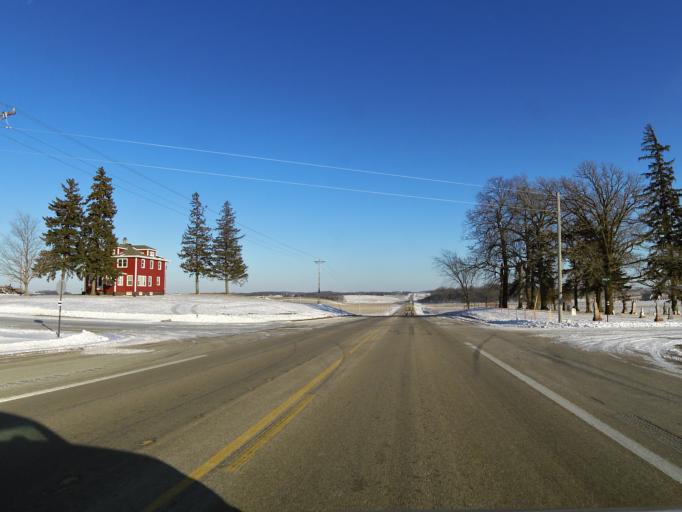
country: US
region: Minnesota
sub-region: Rice County
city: Lonsdale
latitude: 44.4861
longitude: -93.4944
